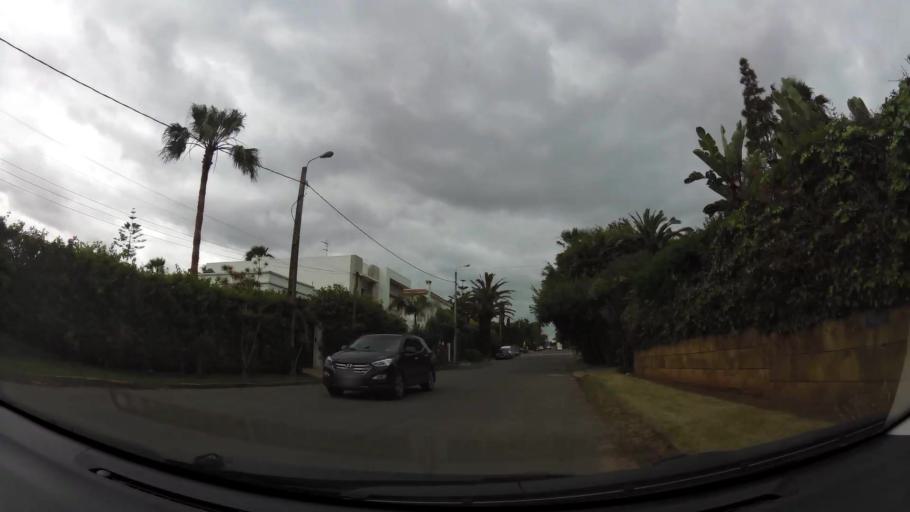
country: MA
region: Grand Casablanca
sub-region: Casablanca
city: Casablanca
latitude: 33.5792
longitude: -7.6606
